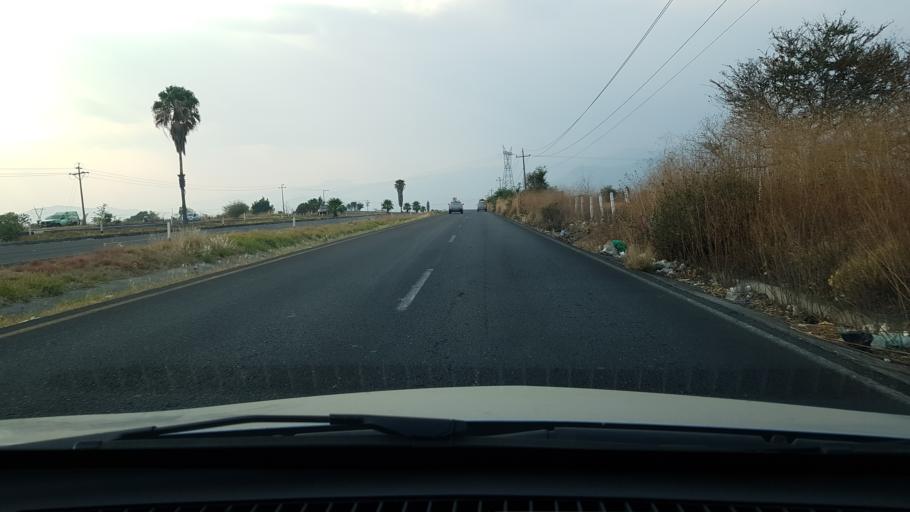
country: MX
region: Morelos
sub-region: Cuautla
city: Narciso Mendoza
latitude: 18.8747
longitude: -98.9583
